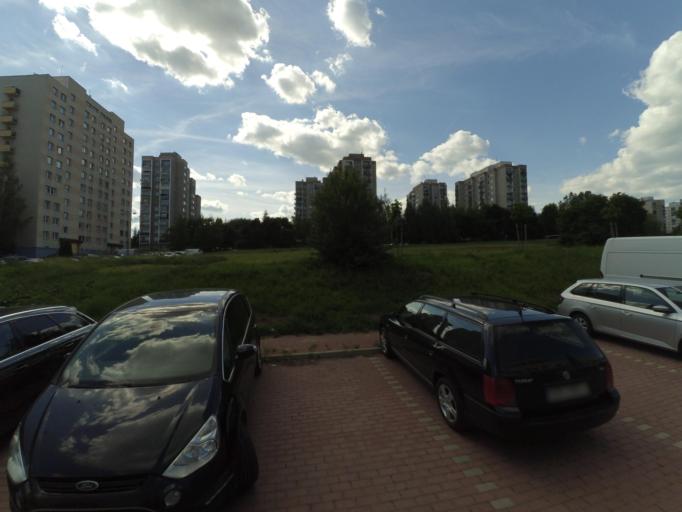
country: PL
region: Lower Silesian Voivodeship
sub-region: Powiat klodzki
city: Klodzko
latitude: 50.4326
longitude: 16.6434
